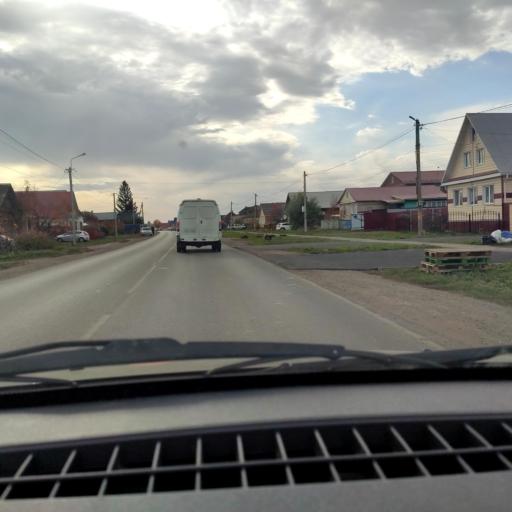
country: RU
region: Bashkortostan
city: Ufa
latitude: 54.6140
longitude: 55.9015
